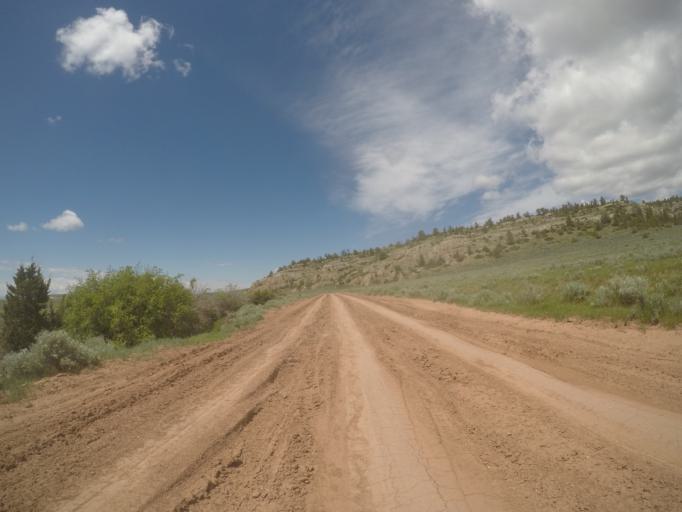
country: US
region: Montana
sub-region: Yellowstone County
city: Laurel
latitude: 45.2430
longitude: -108.6431
